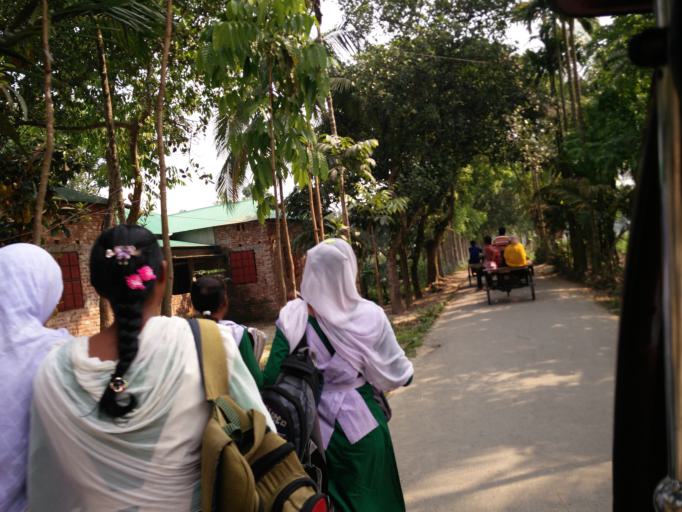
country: BD
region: Dhaka
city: Muktagacha
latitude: 24.9148
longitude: 90.2299
